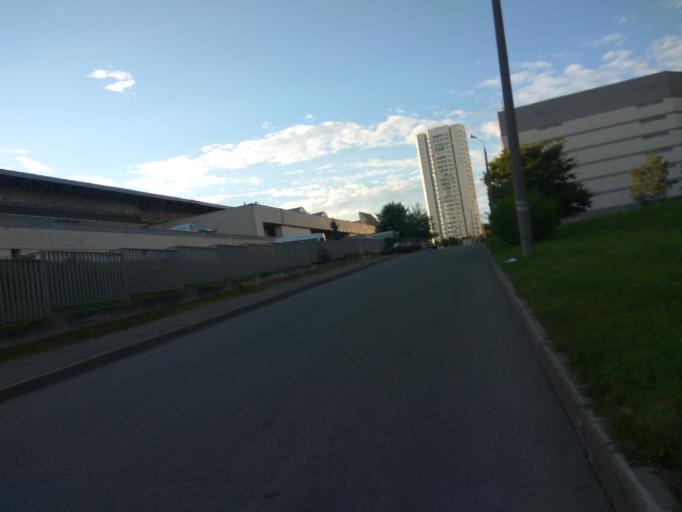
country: RU
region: Moscow
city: Chertanovo Yuzhnoye
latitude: 55.6093
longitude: 37.5776
